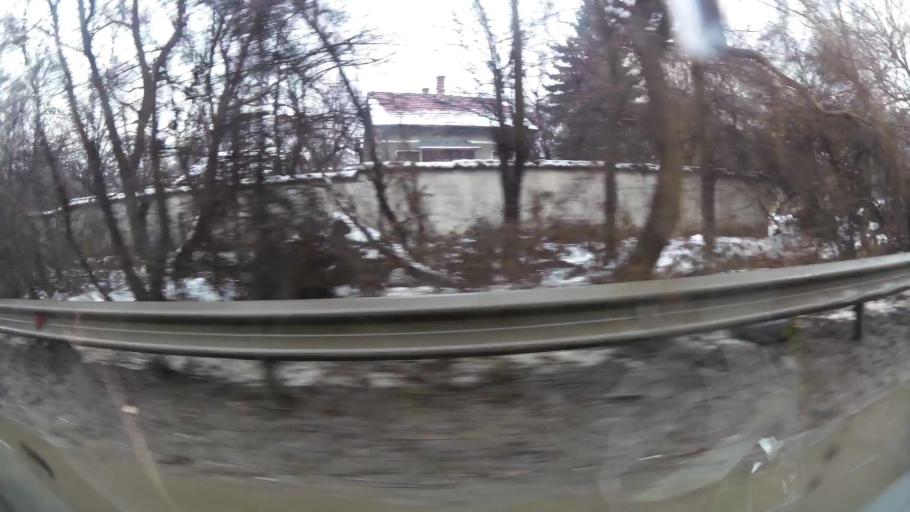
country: BG
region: Sofia-Capital
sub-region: Stolichna Obshtina
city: Sofia
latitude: 42.6628
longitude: 23.2620
